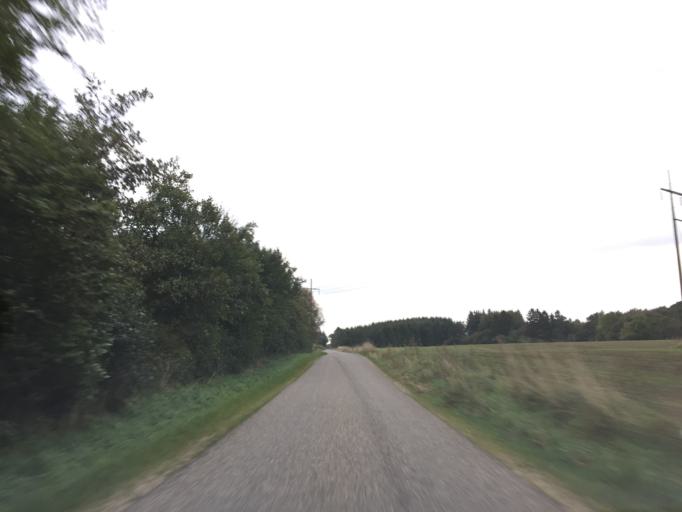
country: DK
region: Central Jutland
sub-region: Viborg Kommune
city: Bjerringbro
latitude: 56.2743
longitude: 9.6873
